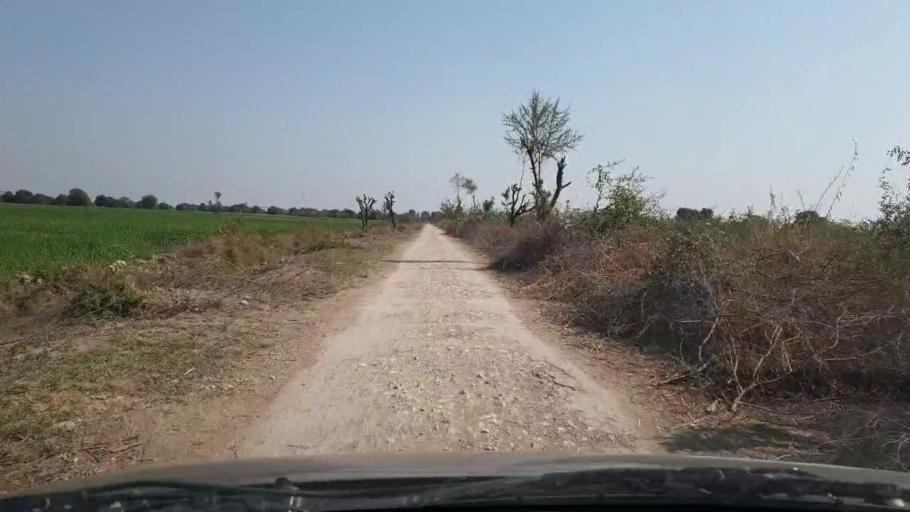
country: PK
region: Sindh
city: Digri
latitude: 25.2036
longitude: 69.2328
